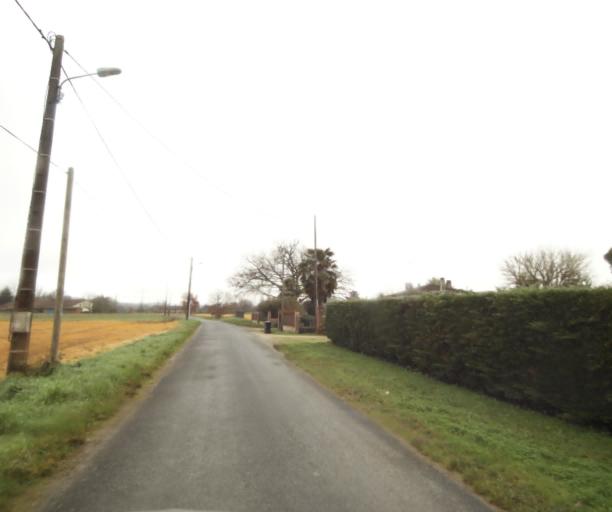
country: FR
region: Midi-Pyrenees
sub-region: Departement du Tarn-et-Garonne
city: Nohic
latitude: 43.8799
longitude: 1.4615
